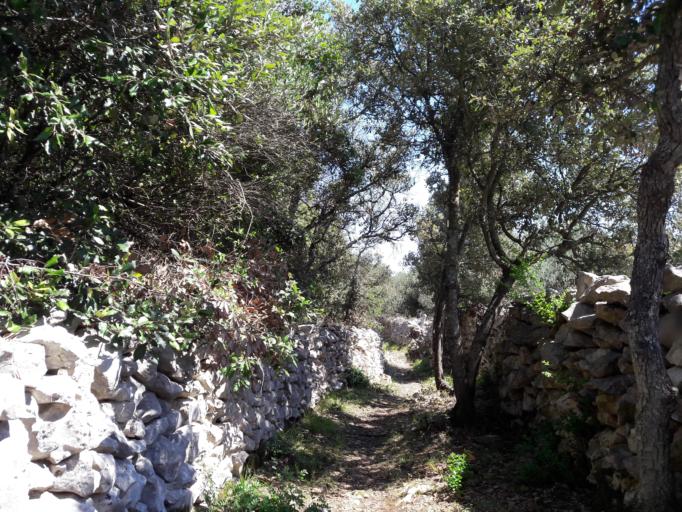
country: HR
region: Licko-Senjska
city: Novalja
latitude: 44.3621
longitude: 14.6973
